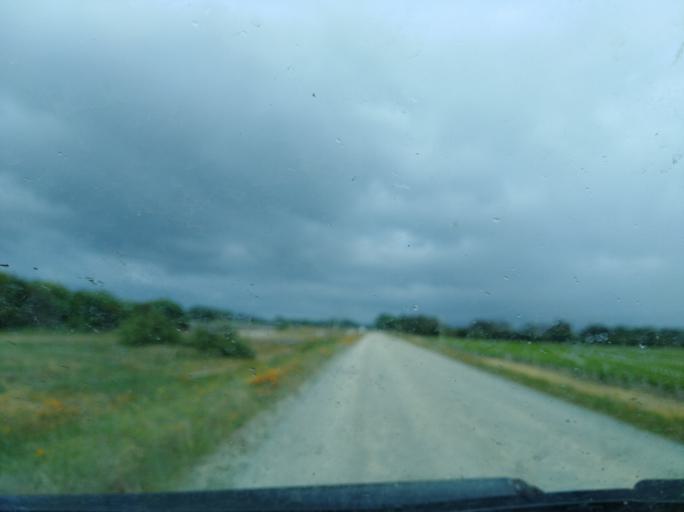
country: NZ
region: Marlborough
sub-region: Marlborough District
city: Blenheim
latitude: -41.4409
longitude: 174.0086
